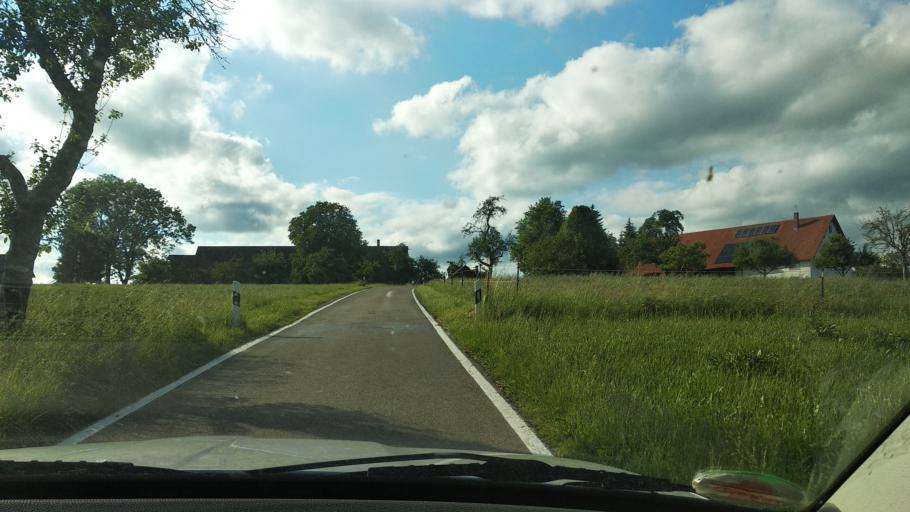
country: DE
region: Baden-Wuerttemberg
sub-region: Tuebingen Region
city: Aitrach
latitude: 47.9479
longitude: 10.0423
